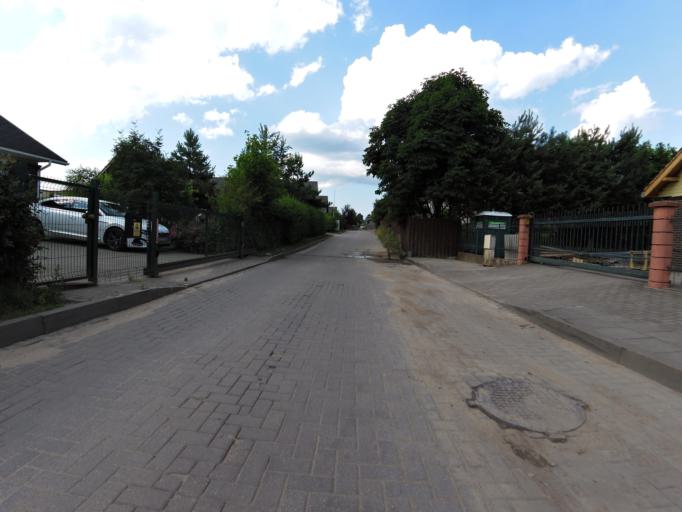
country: LT
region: Vilnius County
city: Pasilaiciai
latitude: 54.7581
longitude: 25.2297
